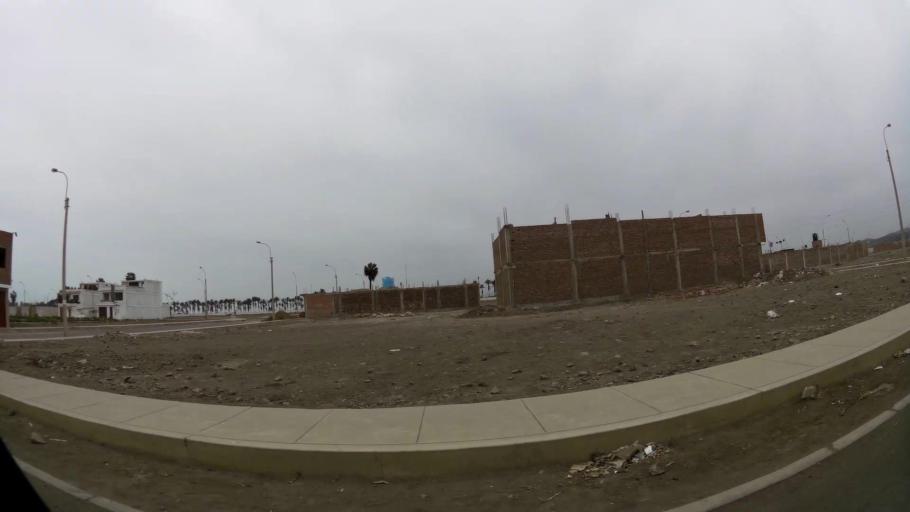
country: PE
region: Lima
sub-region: Barranca
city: Barranca
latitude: -10.7408
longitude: -77.7640
